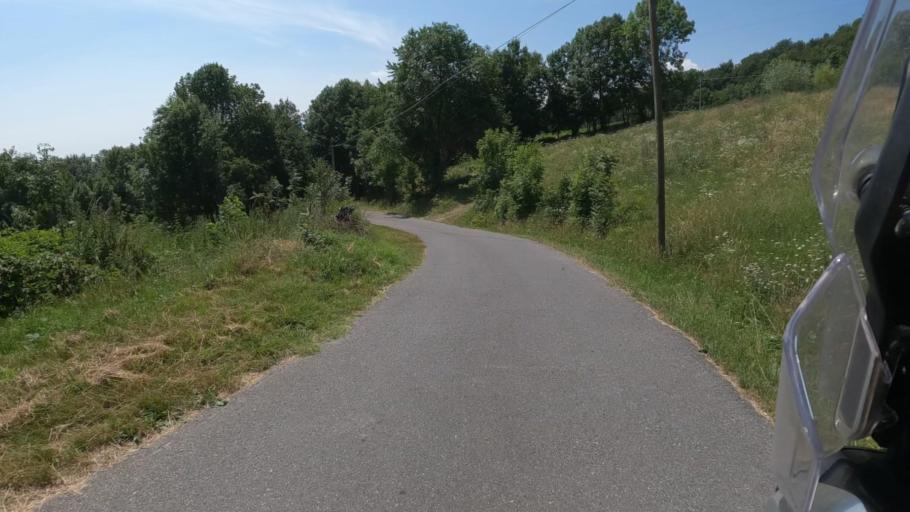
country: IT
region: Piedmont
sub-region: Provincia di Torino
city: Sant'Antonino di Susa
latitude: 45.1434
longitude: 7.2793
